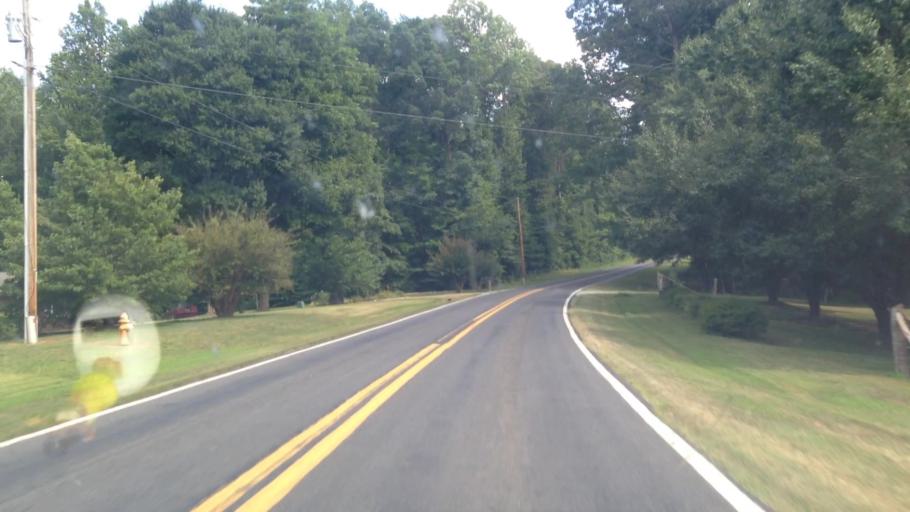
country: US
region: North Carolina
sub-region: Forsyth County
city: Walkertown
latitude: 36.2111
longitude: -80.1105
